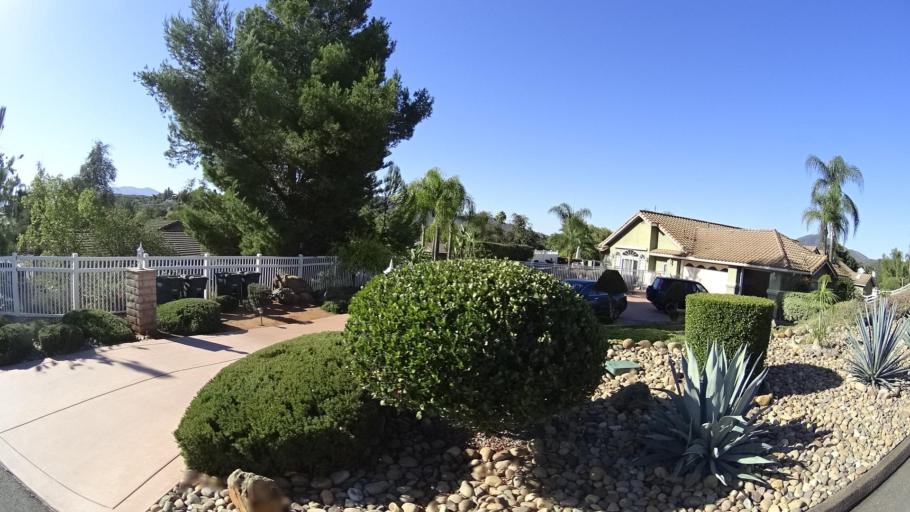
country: US
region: California
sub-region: San Diego County
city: Jamul
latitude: 32.7094
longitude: -116.8780
